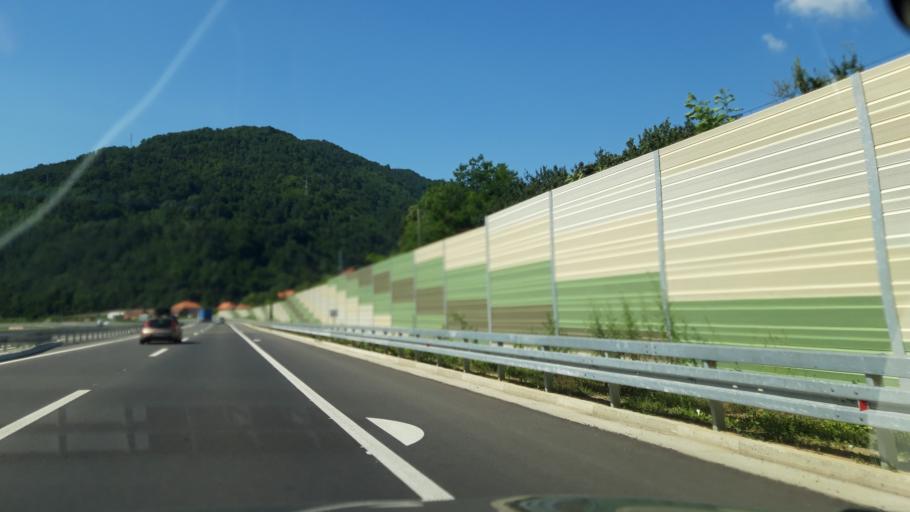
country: RS
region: Central Serbia
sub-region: Jablanicki Okrug
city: Vlasotince
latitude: 42.8589
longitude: 22.1197
